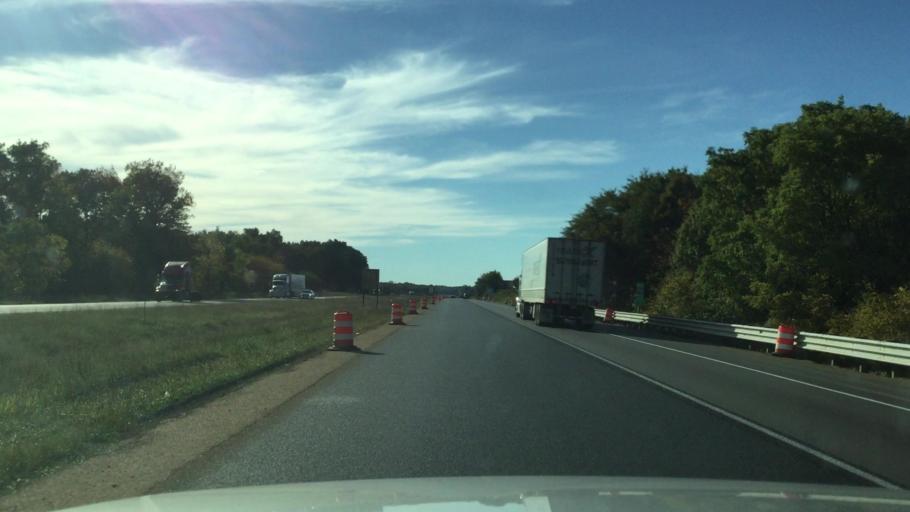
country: US
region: Michigan
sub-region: Calhoun County
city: Marshall
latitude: 42.2827
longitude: -84.8855
